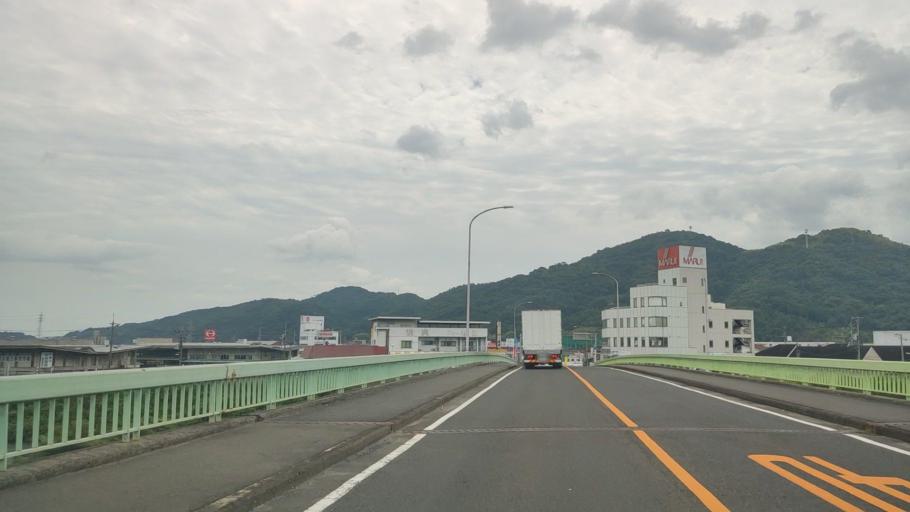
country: JP
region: Okayama
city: Tsuyama
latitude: 35.0591
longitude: 133.9802
